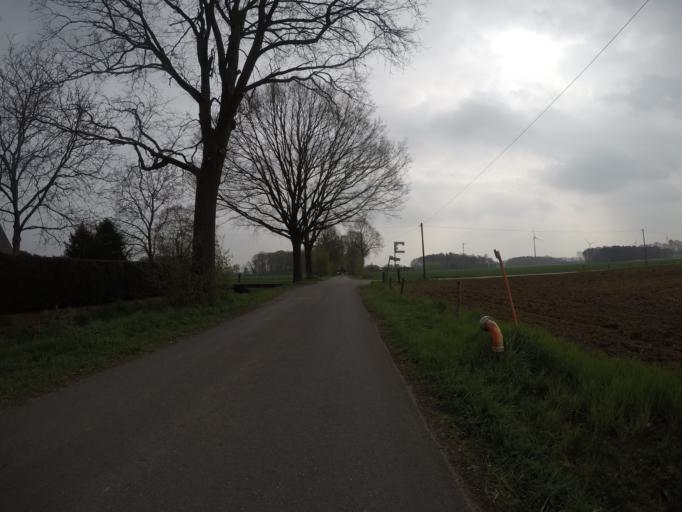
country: NL
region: Gelderland
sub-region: Gemeente Aalten
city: Aalten
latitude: 51.8813
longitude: 6.5603
